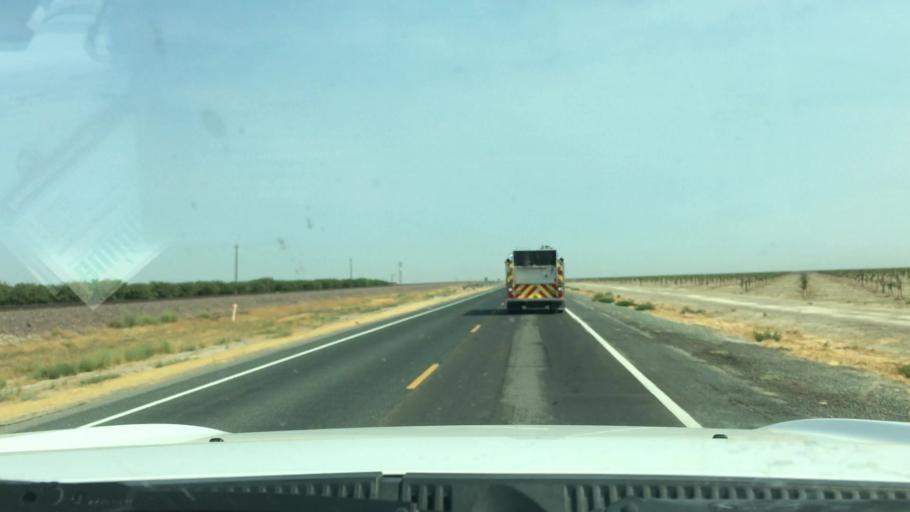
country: US
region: California
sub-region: Kern County
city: Delano
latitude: 35.7869
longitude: -119.3540
